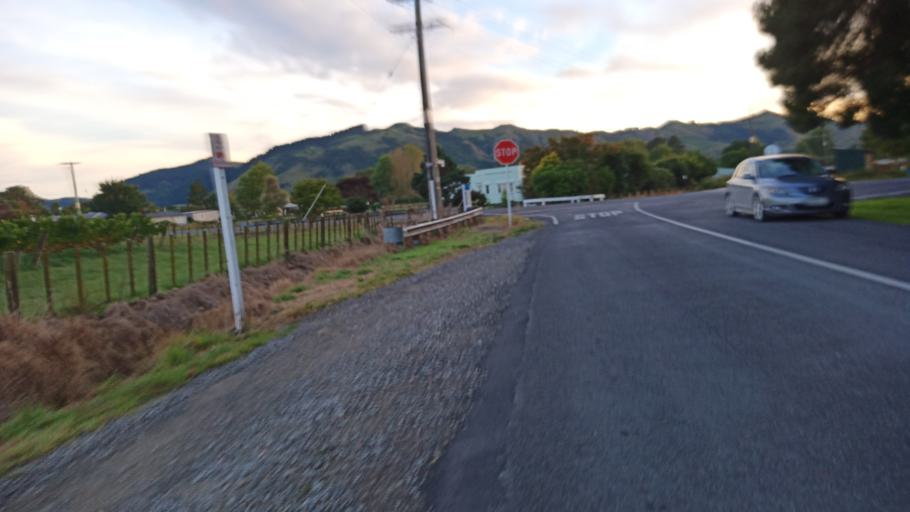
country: NZ
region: Gisborne
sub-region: Gisborne District
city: Gisborne
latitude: -38.6205
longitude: 177.9806
